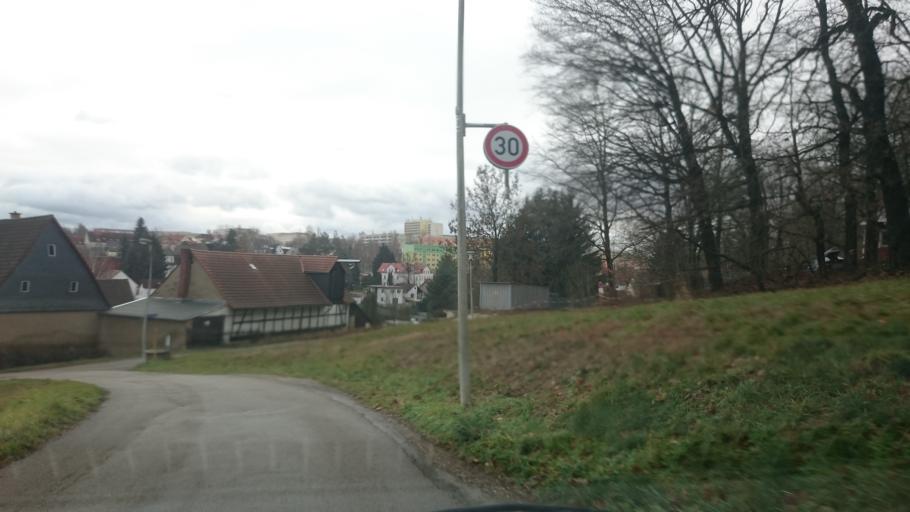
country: DE
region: Saxony
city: Mulsen
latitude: 50.7393
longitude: 12.5287
